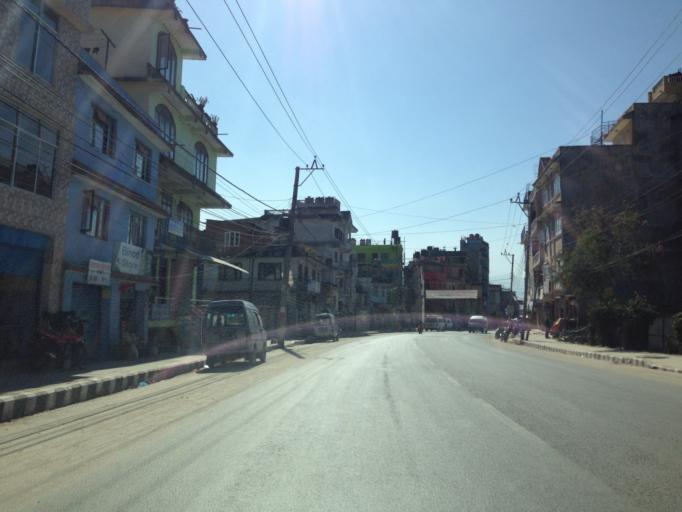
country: NP
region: Central Region
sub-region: Bagmati Zone
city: Kathmandu
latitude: 27.7684
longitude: 85.3564
